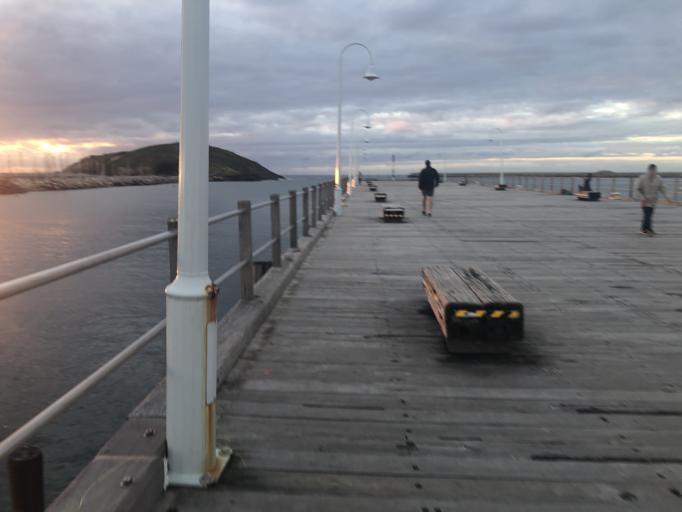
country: AU
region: New South Wales
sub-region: Coffs Harbour
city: Coffs Harbour
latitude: -30.3048
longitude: 153.1430
